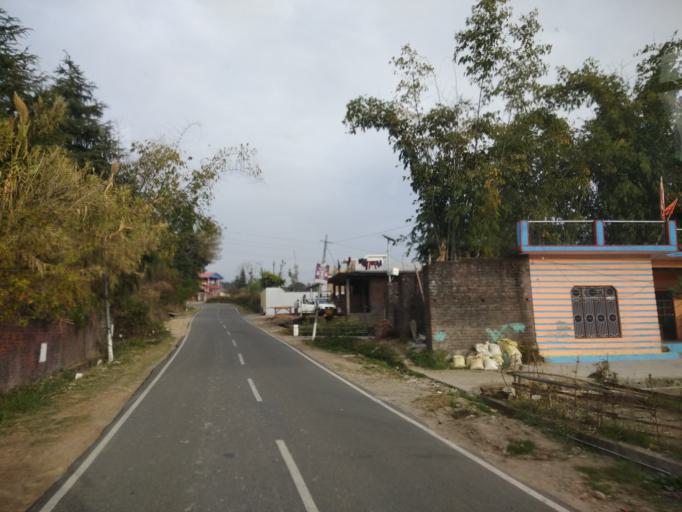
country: IN
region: Himachal Pradesh
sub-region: Kangra
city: Palampur
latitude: 32.1100
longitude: 76.4952
